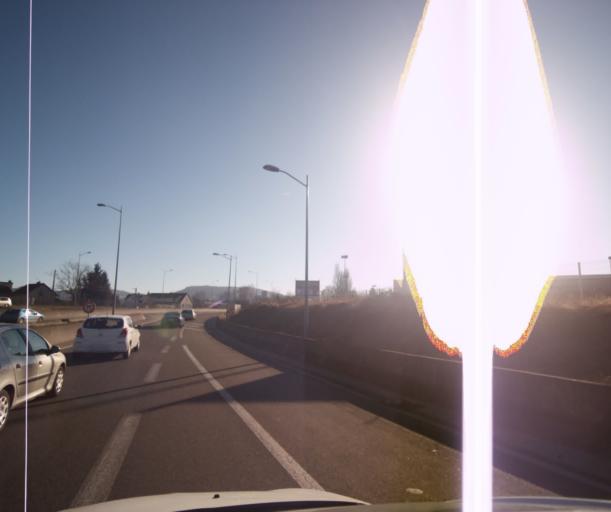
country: FR
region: Franche-Comte
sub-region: Departement du Doubs
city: Pirey
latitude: 47.2322
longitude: 5.9824
